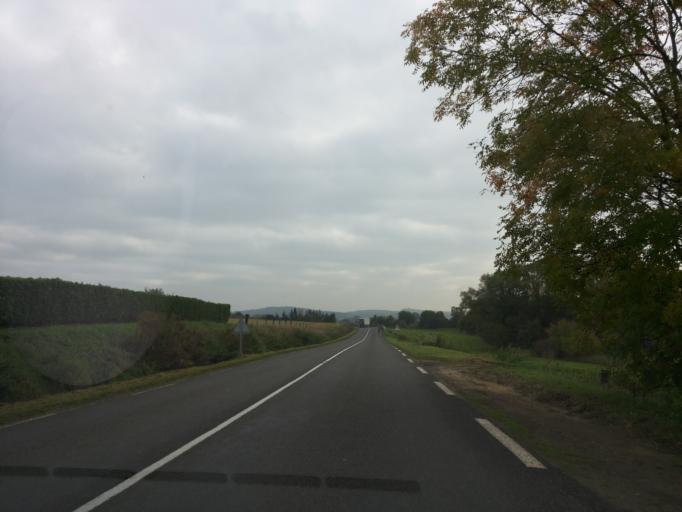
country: FR
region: Champagne-Ardenne
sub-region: Departement des Ardennes
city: Blagny
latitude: 49.6148
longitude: 5.1983
